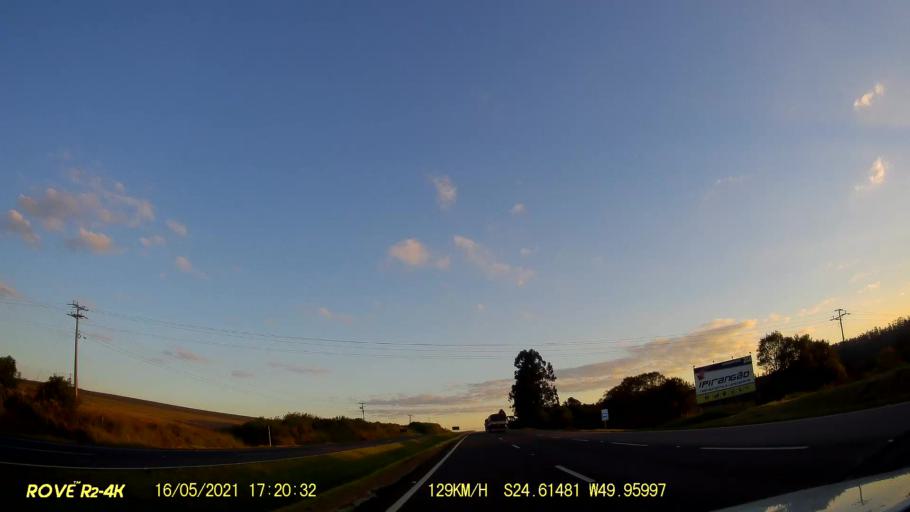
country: BR
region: Parana
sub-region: Pirai Do Sul
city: Pirai do Sul
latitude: -24.6151
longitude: -49.9601
